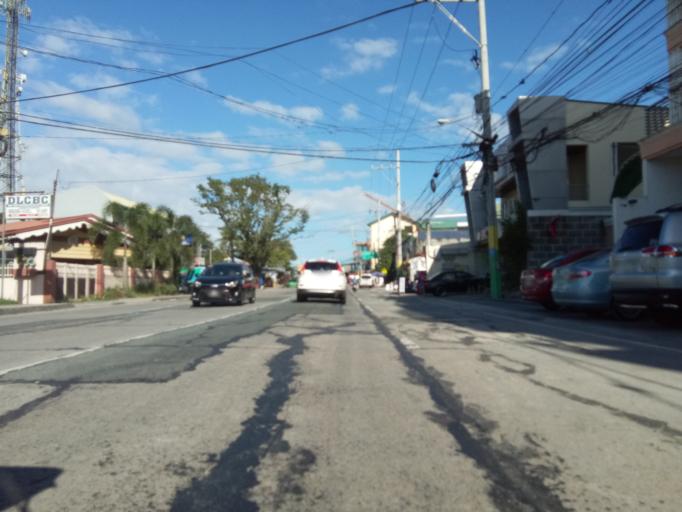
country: PH
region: Calabarzon
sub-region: Province of Cavite
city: Dasmarinas
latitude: 14.3530
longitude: 120.9797
